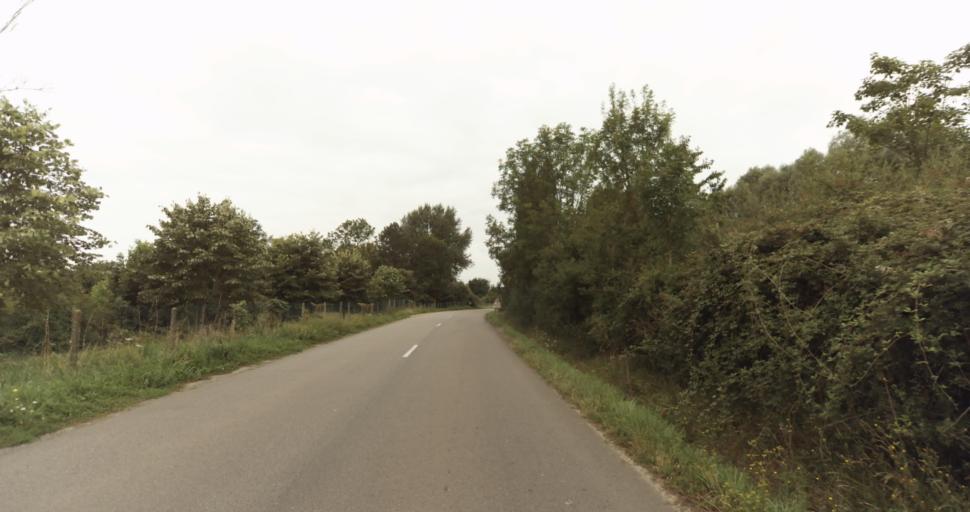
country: FR
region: Haute-Normandie
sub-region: Departement de l'Eure
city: Garennes-sur-Eure
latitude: 48.9177
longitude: 1.4541
